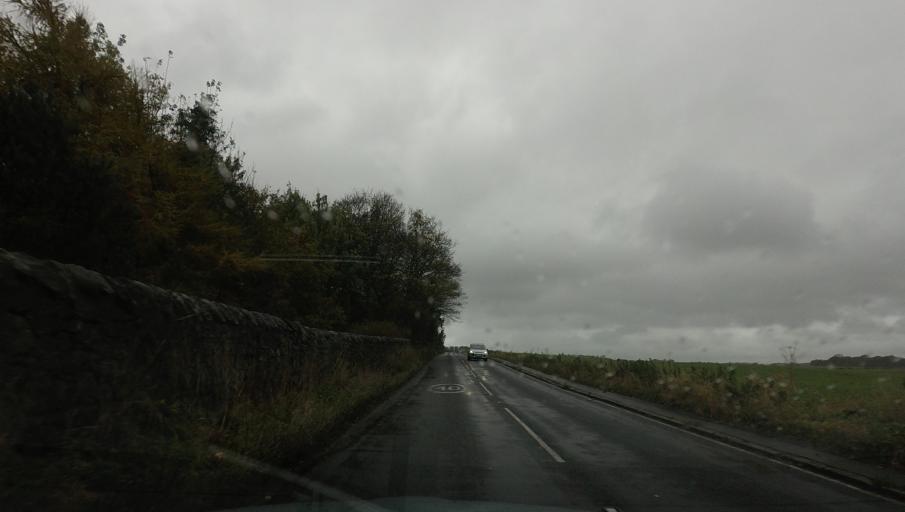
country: GB
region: Scotland
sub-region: Fife
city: East Wemyss
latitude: 56.1558
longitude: -3.0745
